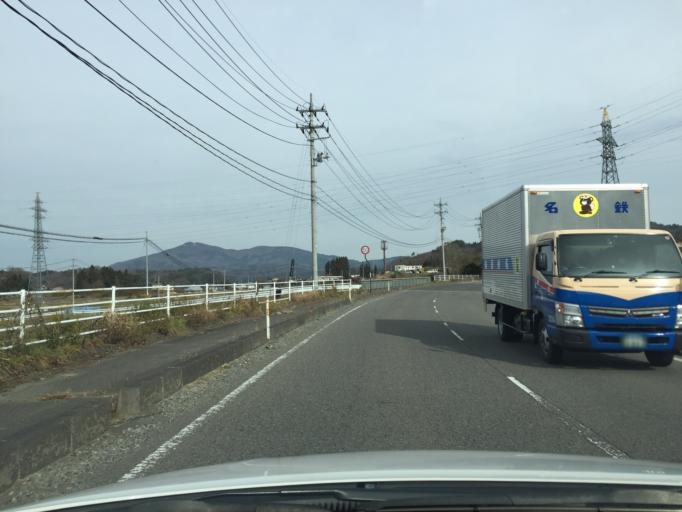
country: JP
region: Fukushima
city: Funehikimachi-funehiki
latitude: 37.4275
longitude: 140.5876
